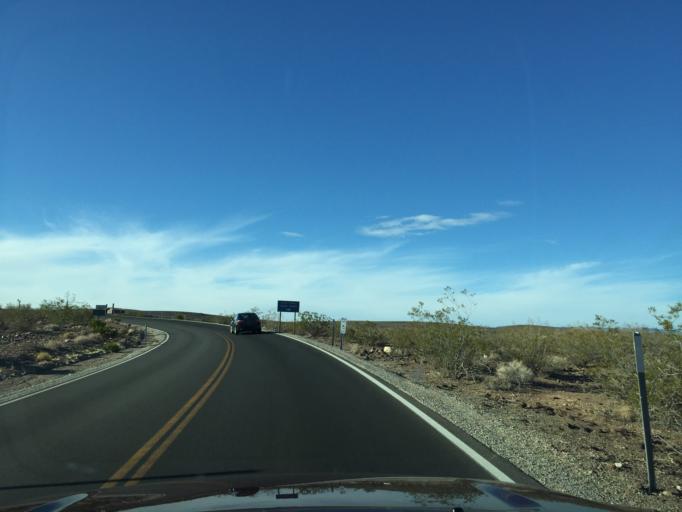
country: US
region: California
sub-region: Inyo County
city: Lone Pine
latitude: 36.3504
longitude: -117.5502
